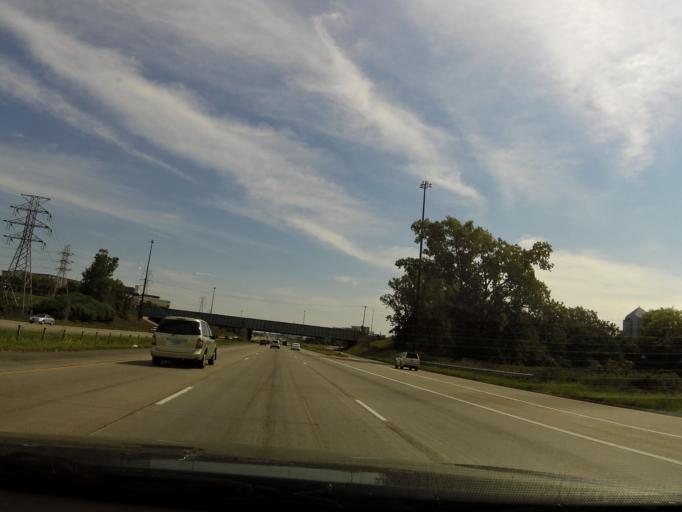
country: US
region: Minnesota
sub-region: Hennepin County
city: Edina
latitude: 44.8597
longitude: -93.3655
